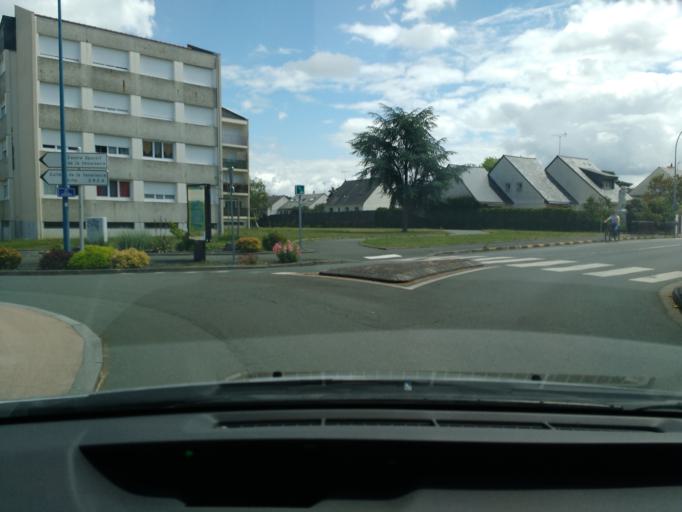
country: FR
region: Pays de la Loire
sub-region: Departement de Maine-et-Loire
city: Trelaze
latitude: 47.4700
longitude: -0.4911
